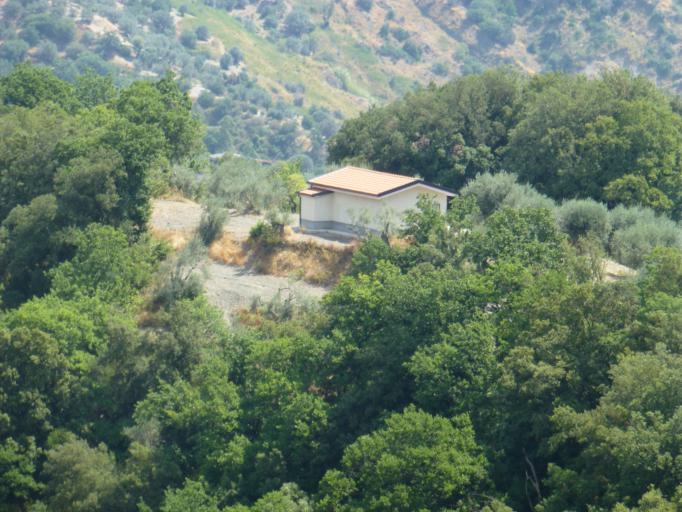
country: IT
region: Calabria
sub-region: Provincia di Reggio Calabria
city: Pazzano
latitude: 38.4805
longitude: 16.4455
